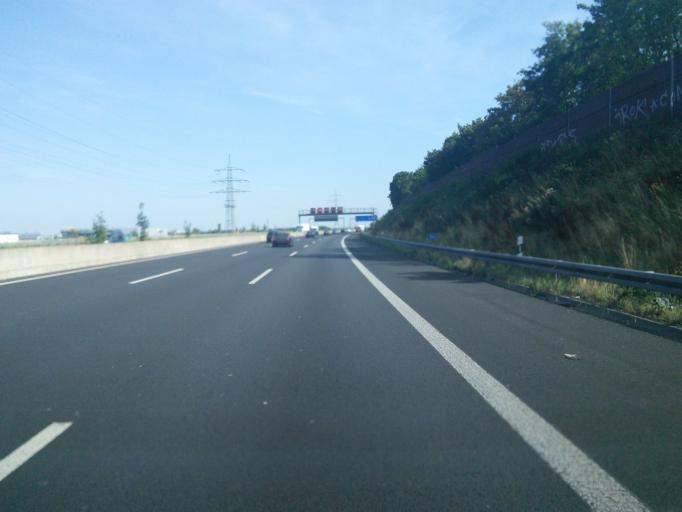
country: DE
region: North Rhine-Westphalia
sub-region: Regierungsbezirk Dusseldorf
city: Neuss
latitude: 51.1677
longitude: 6.7377
